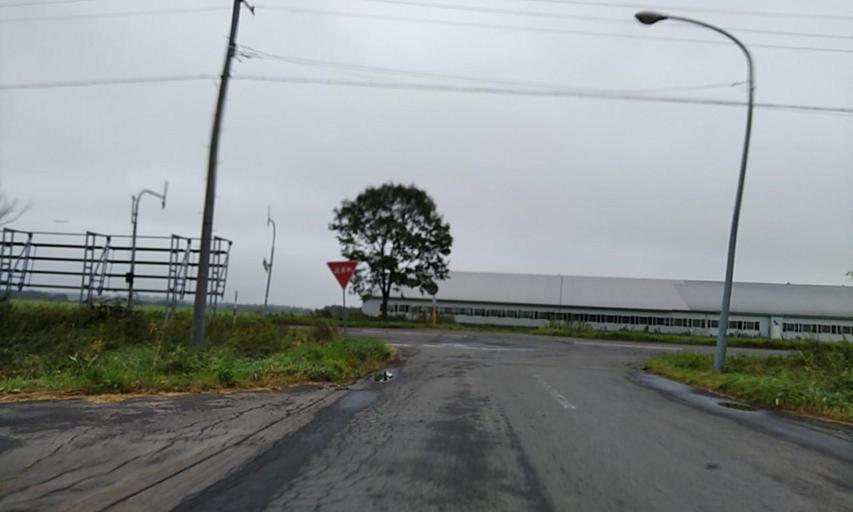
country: JP
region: Hokkaido
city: Shibetsu
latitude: 43.5370
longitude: 144.7093
